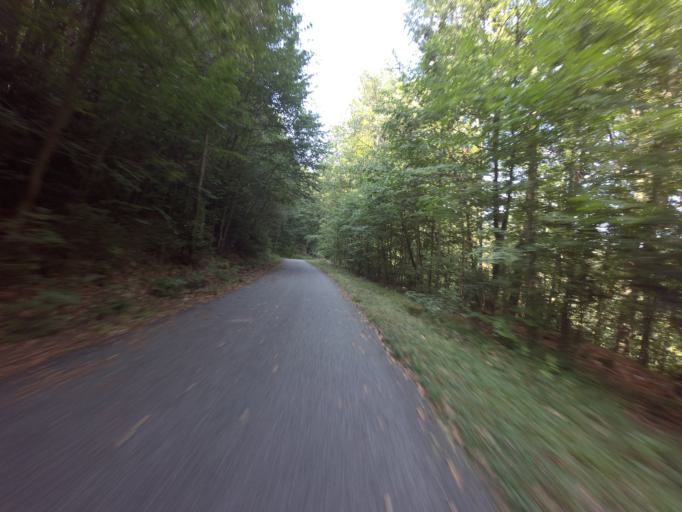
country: CZ
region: Jihocesky
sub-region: Okres Ceske Budejovice
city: Hluboka nad Vltavou
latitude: 49.0935
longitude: 14.4621
